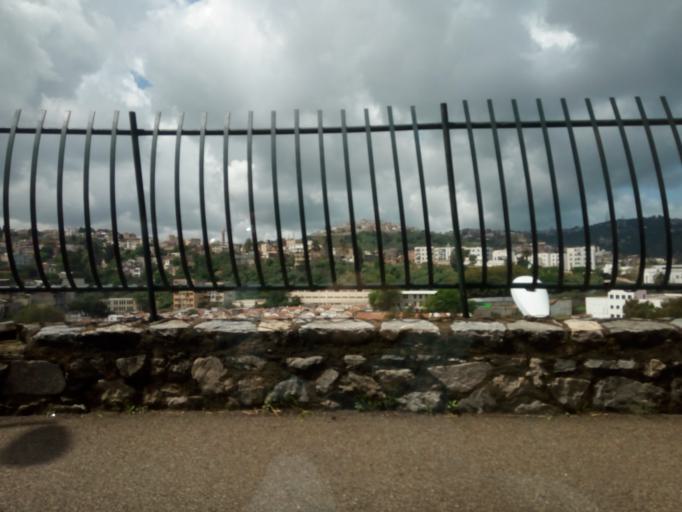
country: DZ
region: Alger
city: Algiers
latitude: 36.7799
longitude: 3.0491
